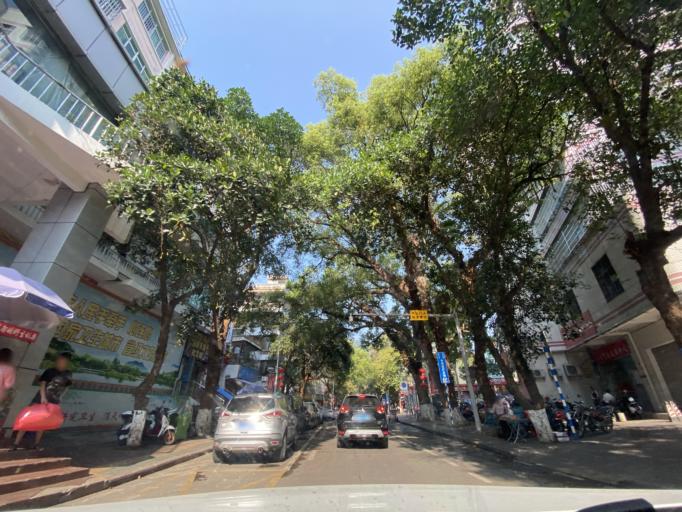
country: CN
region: Hainan
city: Chongshan
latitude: 18.7792
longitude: 109.5114
